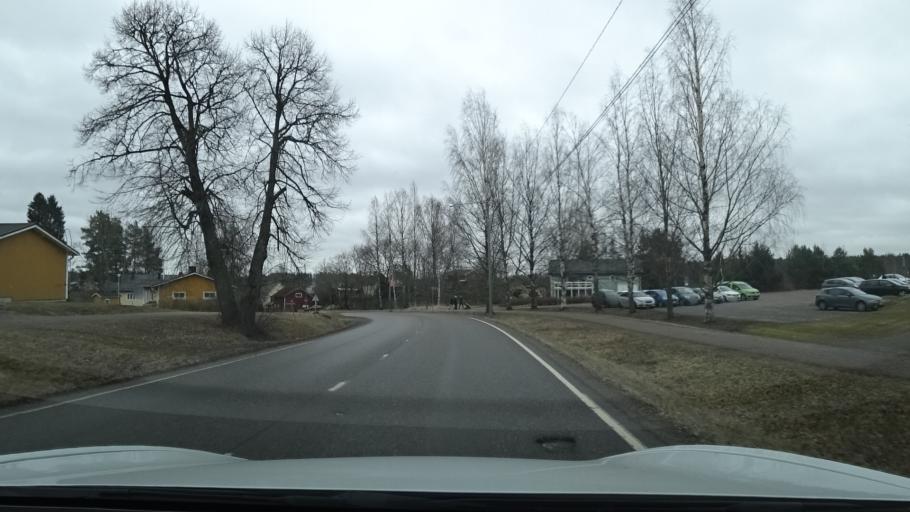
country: FI
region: Uusimaa
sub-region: Porvoo
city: Askola
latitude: 60.4945
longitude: 25.5373
